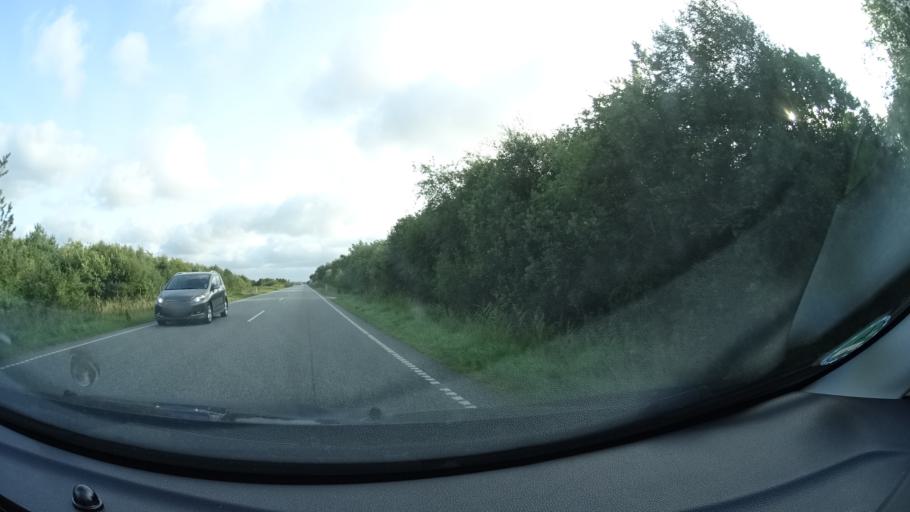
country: DK
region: Central Jutland
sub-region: Lemvig Kommune
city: Harboore
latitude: 56.6148
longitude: 8.1860
